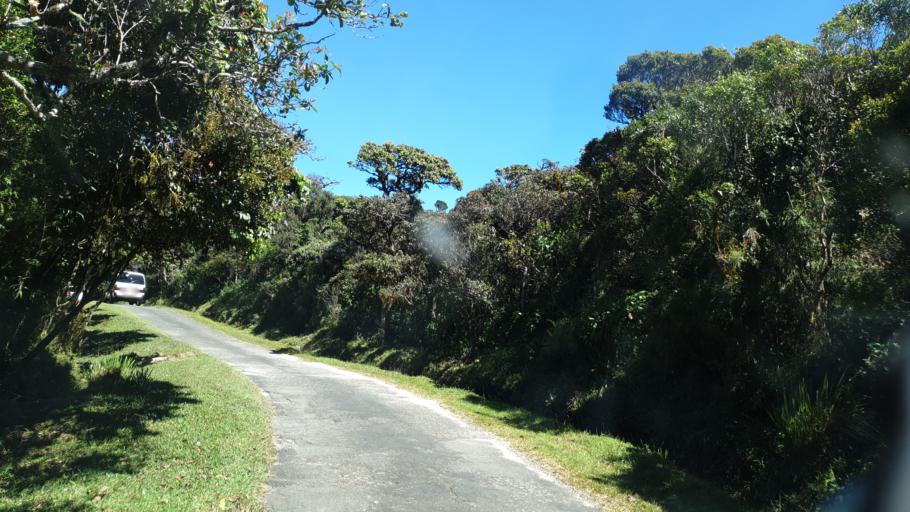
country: LK
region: Uva
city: Haputale
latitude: 6.8044
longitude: 80.8331
